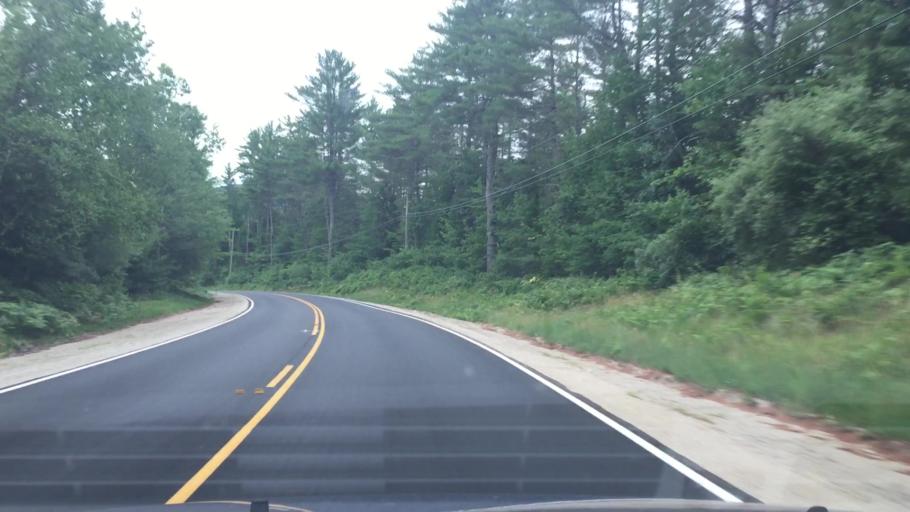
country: US
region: New Hampshire
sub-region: Carroll County
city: Freedom
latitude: 43.8092
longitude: -71.0658
